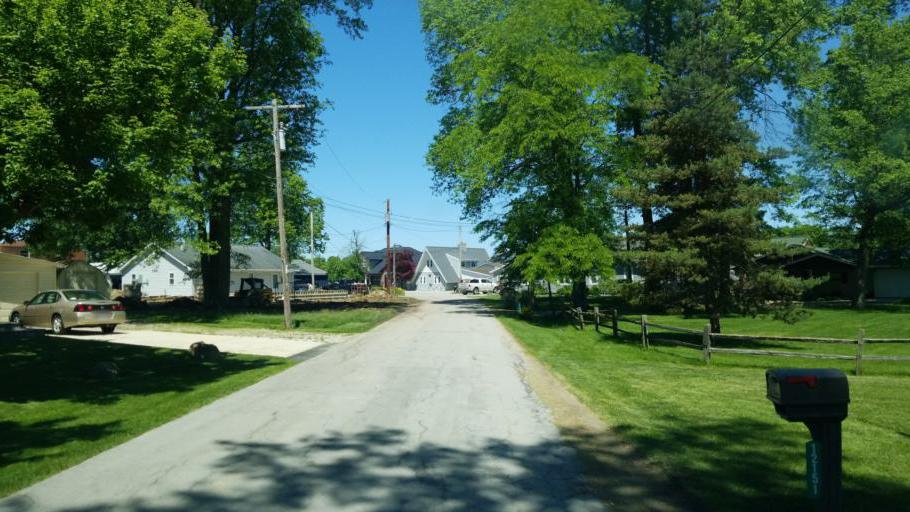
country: US
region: Ohio
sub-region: Shelby County
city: Fort Loramie
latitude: 40.3697
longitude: -84.3419
